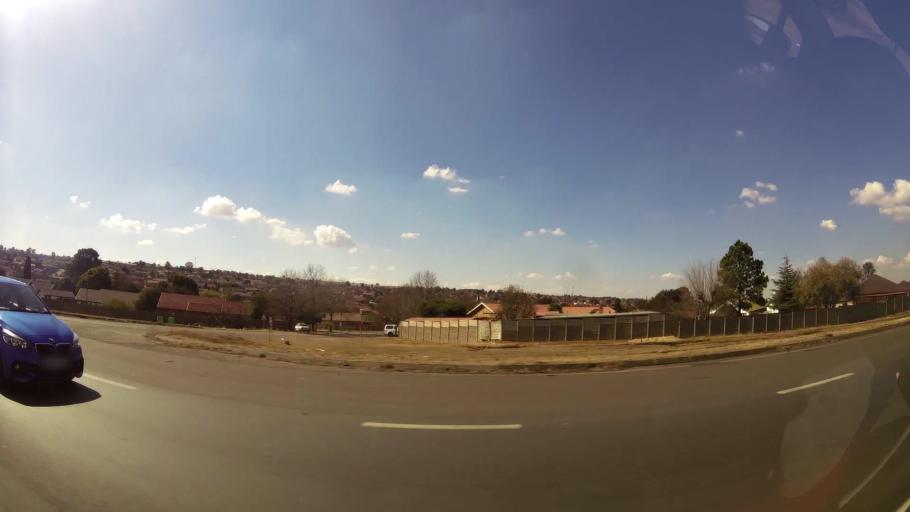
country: ZA
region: Mpumalanga
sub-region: Nkangala District Municipality
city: Witbank
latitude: -25.9347
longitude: 29.2380
